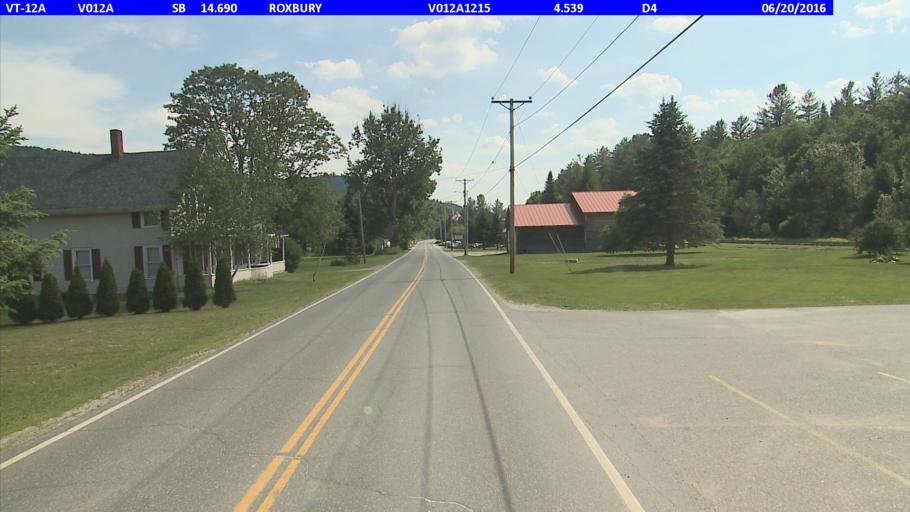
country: US
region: Vermont
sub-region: Washington County
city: Northfield
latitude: 44.0909
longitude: -72.7339
